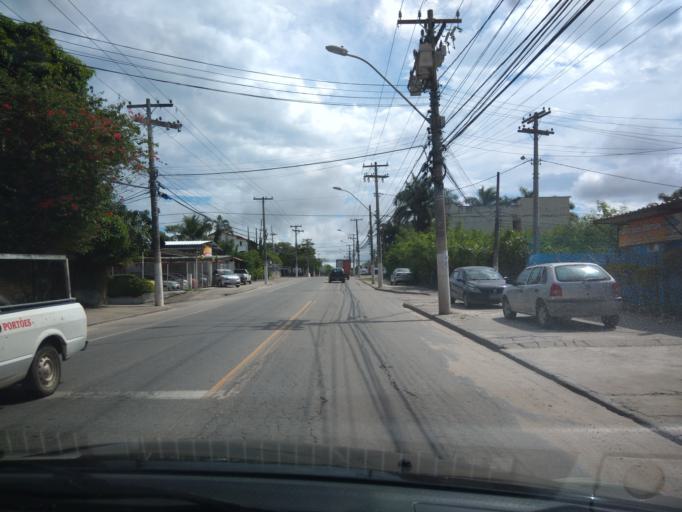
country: BR
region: Rio de Janeiro
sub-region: Niteroi
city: Niteroi
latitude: -22.9331
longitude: -43.0201
